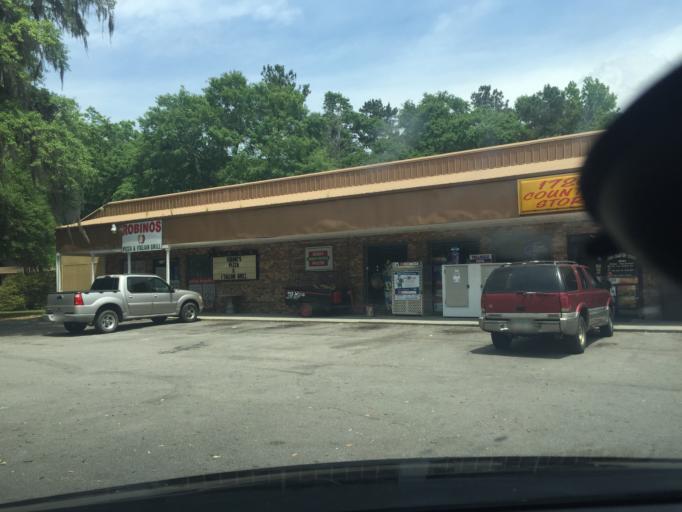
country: US
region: Georgia
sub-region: Chatham County
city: Bloomingdale
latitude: 32.1464
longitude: -81.3391
